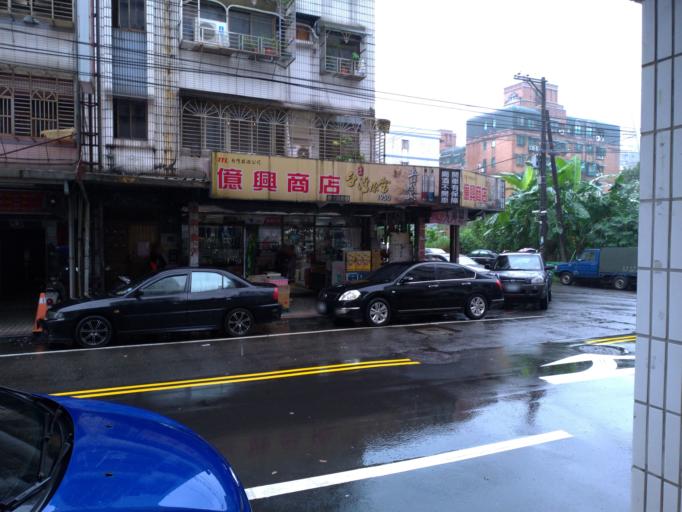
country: TW
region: Taiwan
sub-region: Keelung
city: Keelung
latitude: 25.0844
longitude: 121.6962
